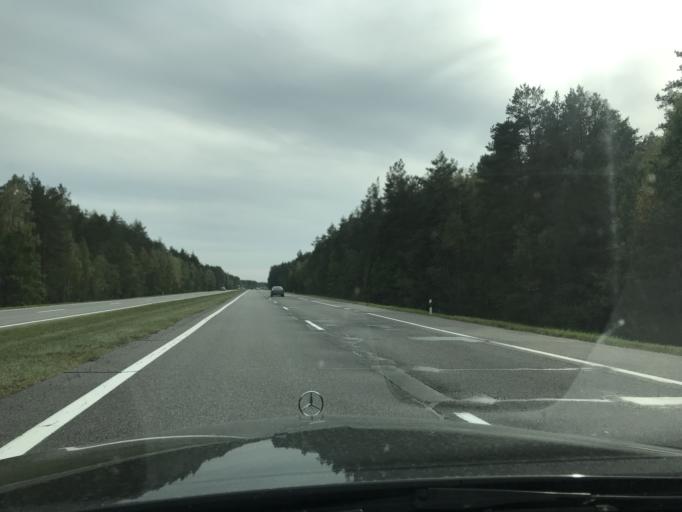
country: BY
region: Grodnenskaya
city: Zhyrovichy
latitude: 52.8723
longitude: 25.6584
